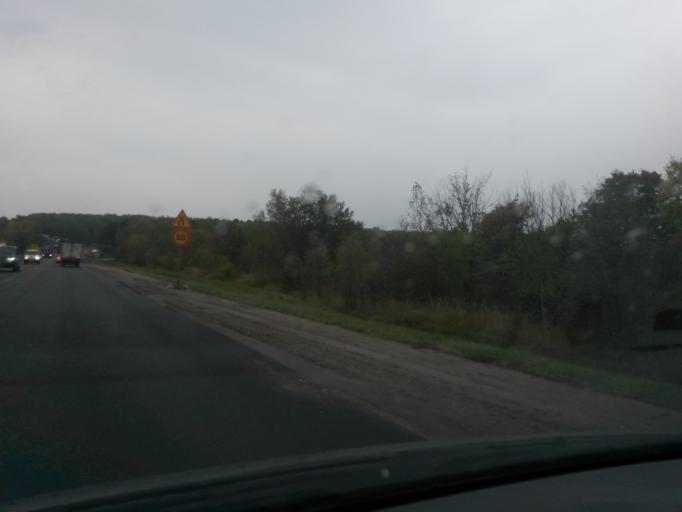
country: RU
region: Nizjnij Novgorod
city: Pamyat' Parizhskoy Kommuny
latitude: 56.0729
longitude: 44.3722
